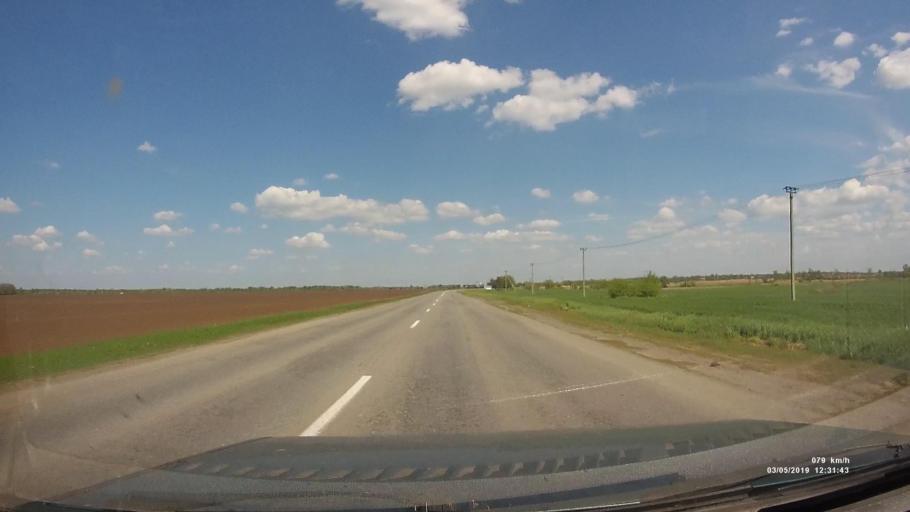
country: RU
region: Rostov
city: Semikarakorsk
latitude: 47.5065
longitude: 40.7501
